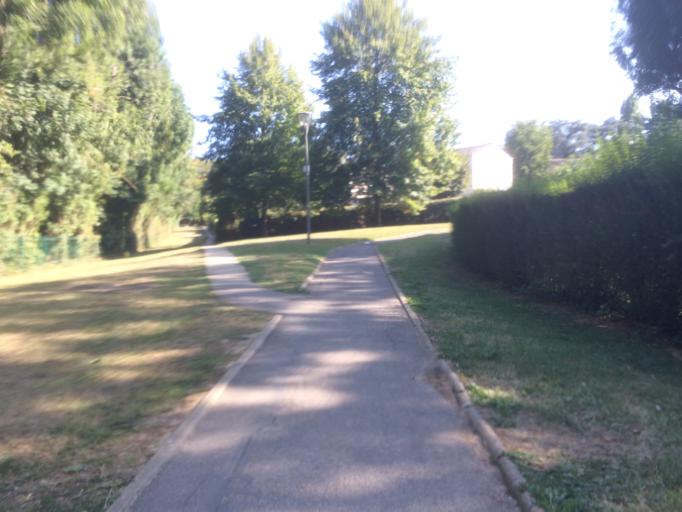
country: FR
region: Ile-de-France
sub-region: Departement de l'Essonne
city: Epinay-sur-Orge
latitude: 48.6837
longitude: 2.3190
